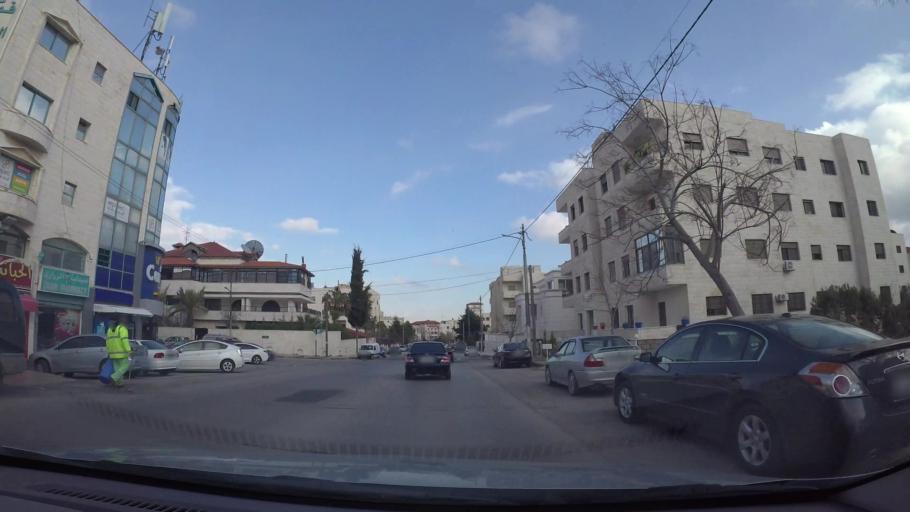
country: JO
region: Amman
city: Wadi as Sir
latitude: 31.9791
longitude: 35.8510
